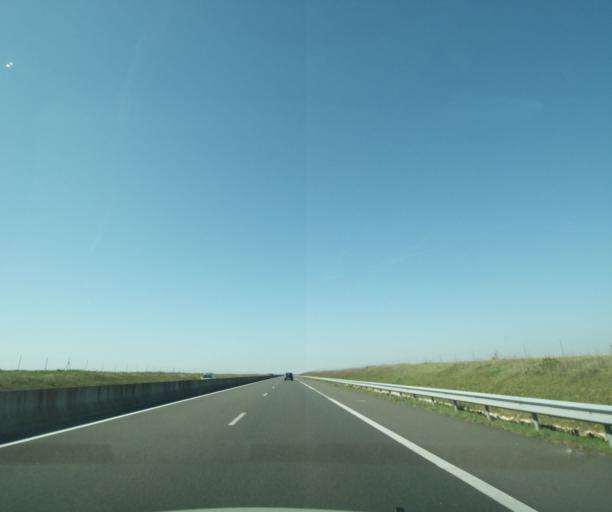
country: FR
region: Centre
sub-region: Departement du Loiret
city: Ascheres-le-Marche
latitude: 48.0668
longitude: 1.9587
